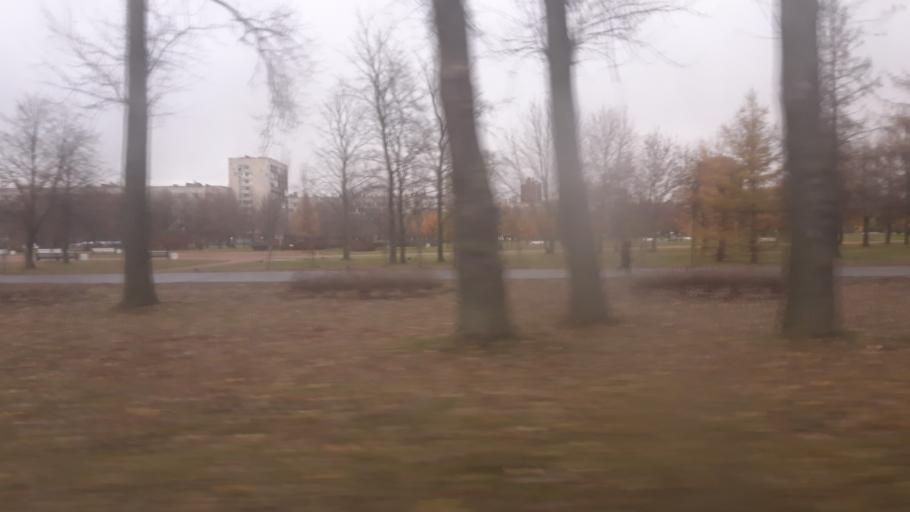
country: RU
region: St.-Petersburg
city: Kupchino
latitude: 59.8397
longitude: 30.3225
